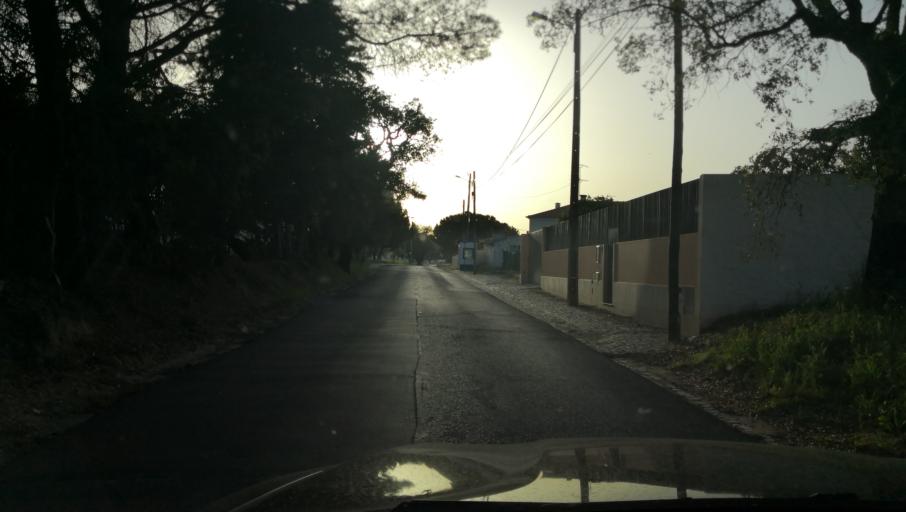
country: PT
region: Setubal
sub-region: Setubal
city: Setubal
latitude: 38.5364
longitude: -8.8216
